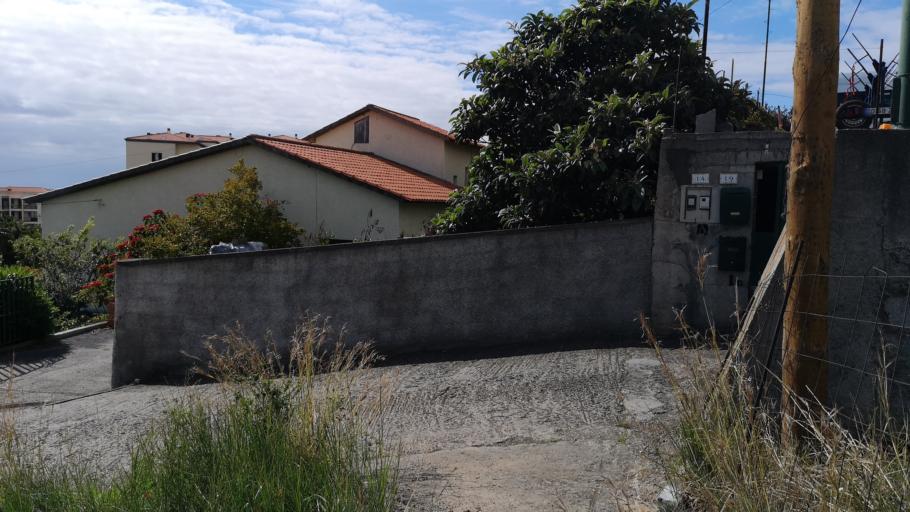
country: PT
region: Madeira
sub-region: Santa Cruz
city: Camacha
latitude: 32.6568
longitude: -16.8291
